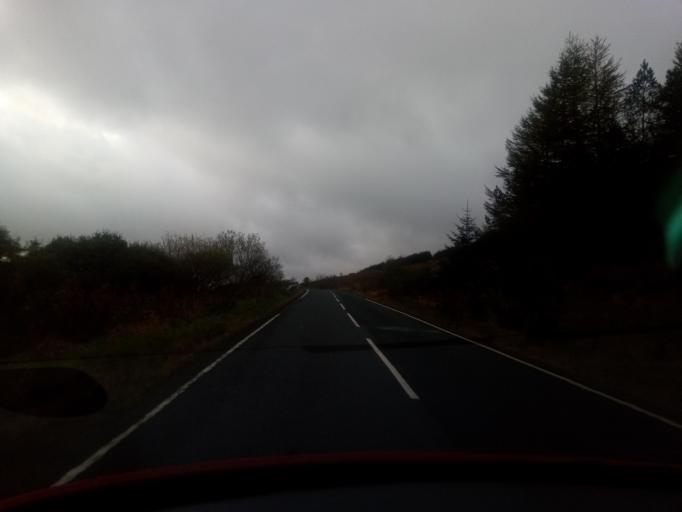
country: GB
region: Scotland
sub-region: The Scottish Borders
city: Hawick
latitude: 55.3239
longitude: -2.6467
